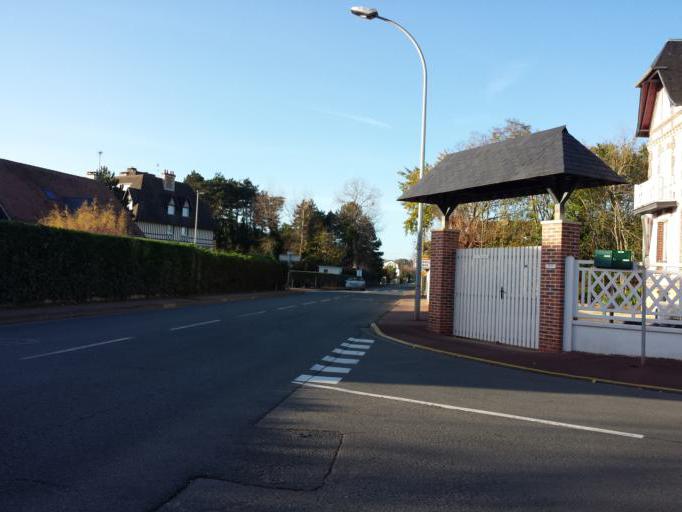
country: FR
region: Lower Normandy
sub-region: Departement du Calvados
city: Deauville
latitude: 49.3504
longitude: 0.0549
